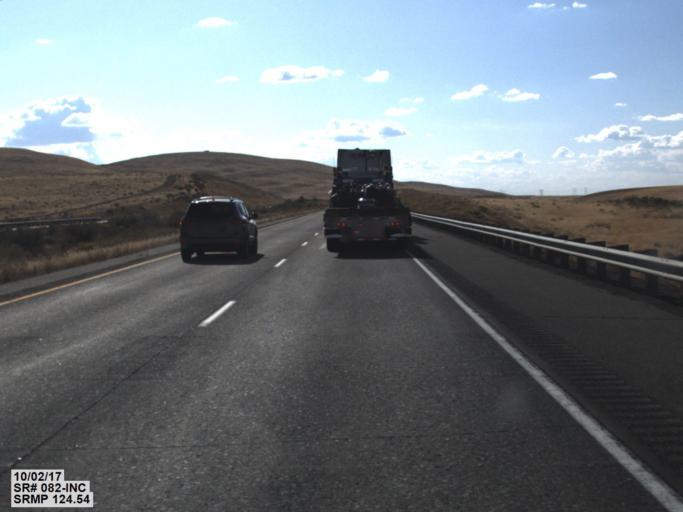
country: US
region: Oregon
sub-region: Umatilla County
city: Umatilla
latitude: 46.0057
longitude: -119.2459
